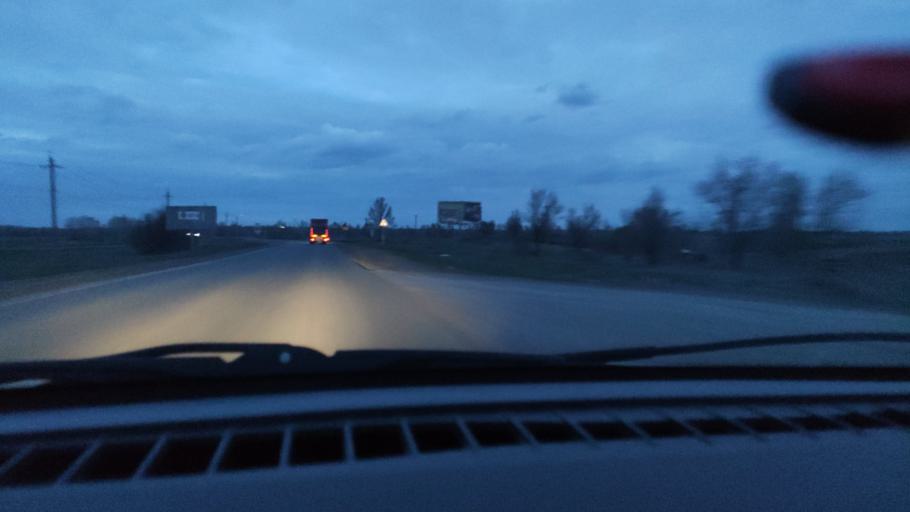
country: RU
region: Orenburg
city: Tatarskaya Kargala
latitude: 51.9115
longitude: 55.1733
